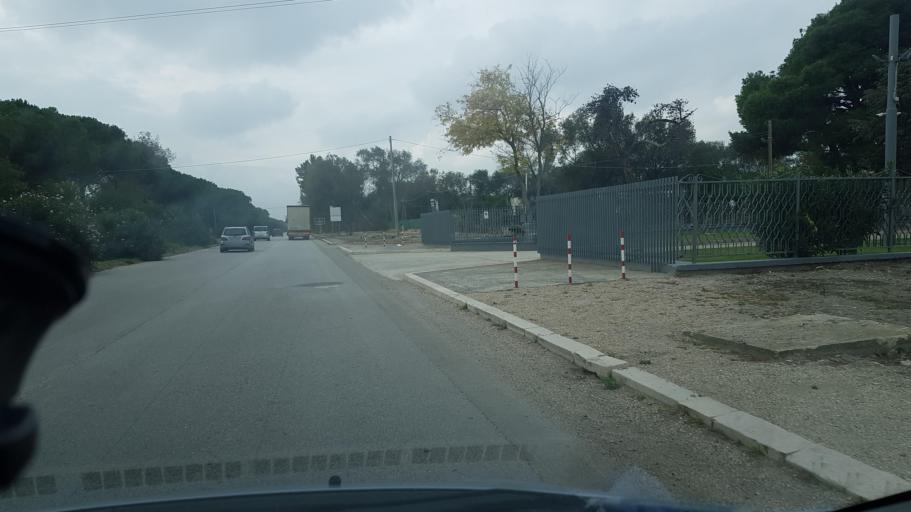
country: IT
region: Apulia
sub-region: Provincia di Foggia
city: Foggia
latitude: 41.4860
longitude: 15.5632
